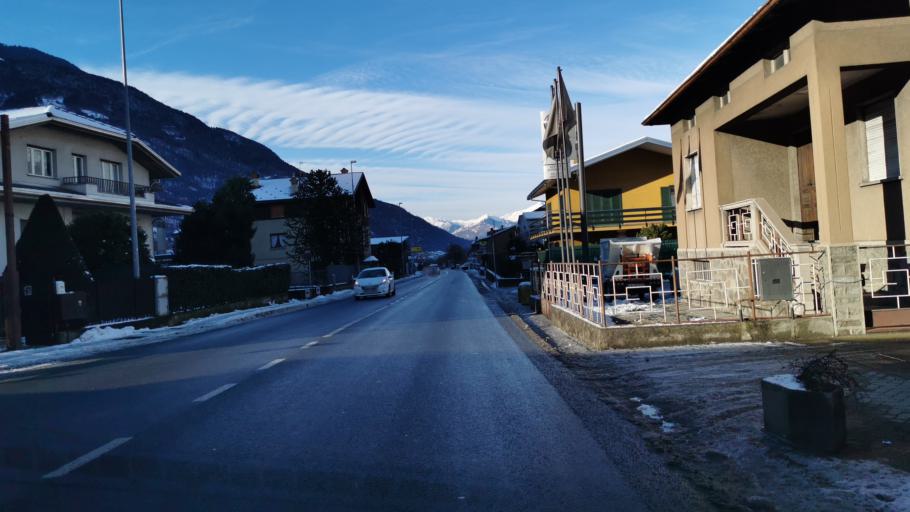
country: IT
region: Lombardy
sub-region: Provincia di Sondrio
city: Cosio Valtellino
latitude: 46.1337
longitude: 9.5512
